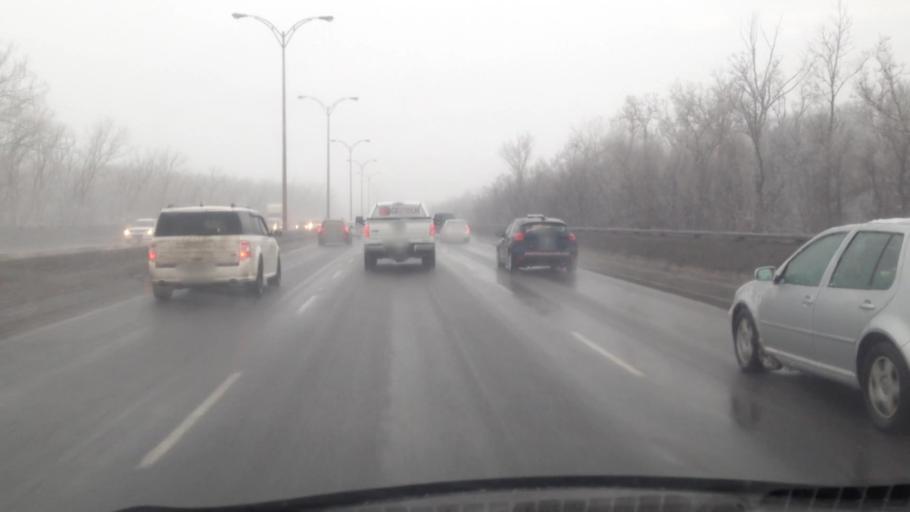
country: CA
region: Quebec
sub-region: Laurentides
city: Boisbriand
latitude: 45.6103
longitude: -73.8128
